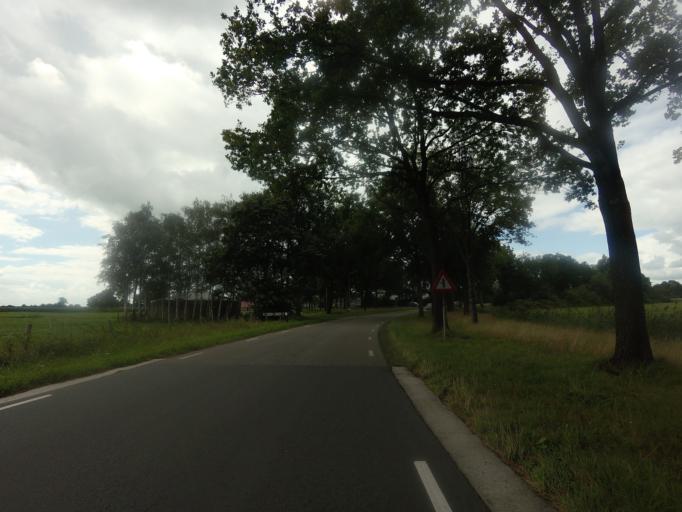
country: NL
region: Drenthe
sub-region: Gemeente Meppel
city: Meppel
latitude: 52.6781
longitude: 6.2192
